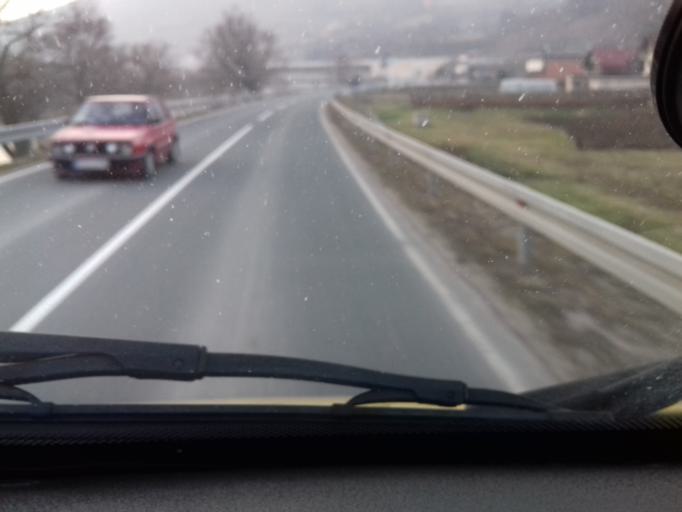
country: BA
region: Federation of Bosnia and Herzegovina
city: Kacuni
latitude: 44.1329
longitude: 17.9970
